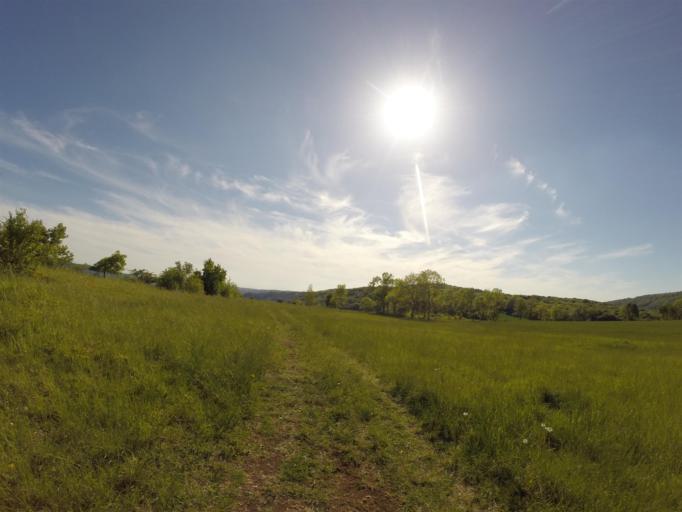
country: DE
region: Thuringia
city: Neuengonna
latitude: 50.9819
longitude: 11.6472
